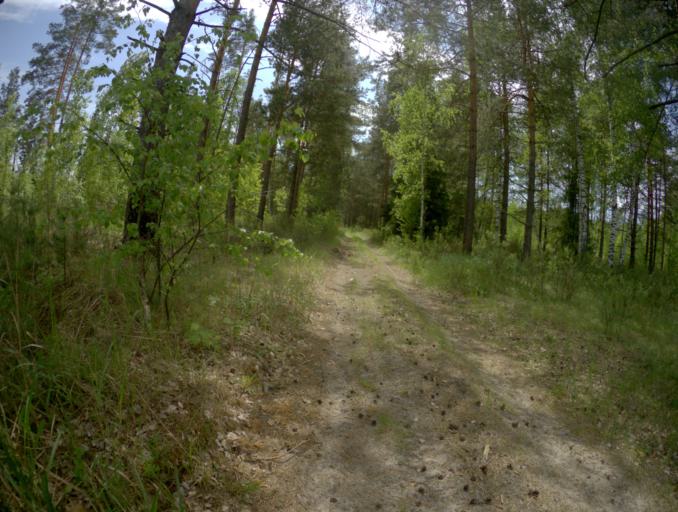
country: RU
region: Vladimir
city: Ivanishchi
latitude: 55.7043
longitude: 40.4658
